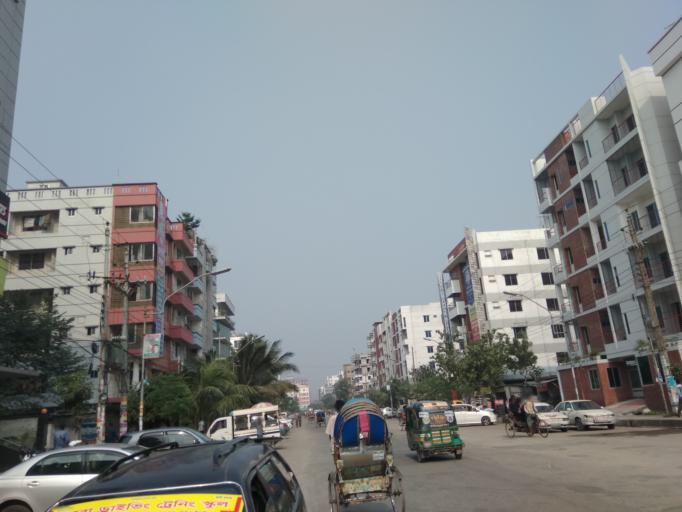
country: BD
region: Dhaka
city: Tungi
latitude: 23.8708
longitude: 90.3839
